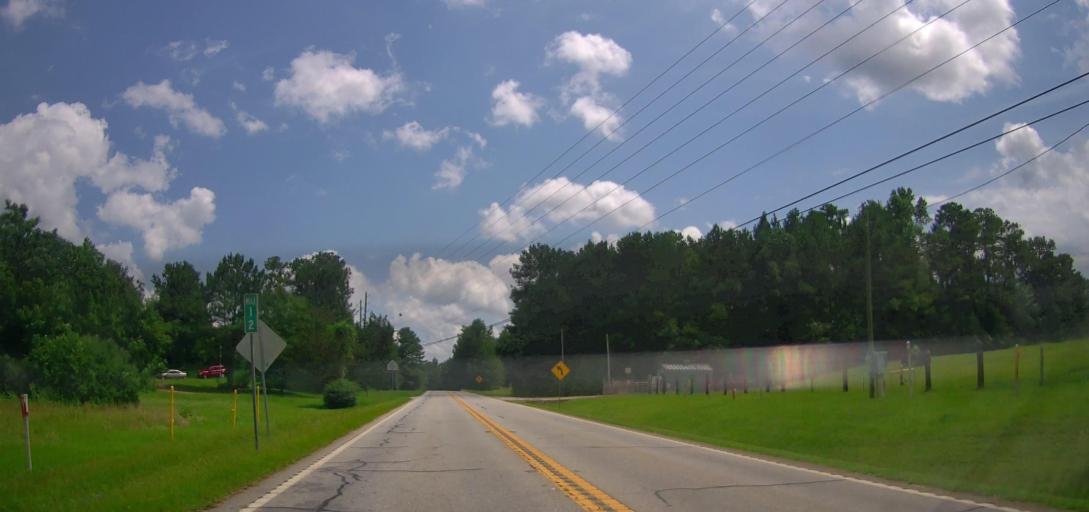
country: US
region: Georgia
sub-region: Heard County
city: Franklin
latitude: 33.2924
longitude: -85.1188
